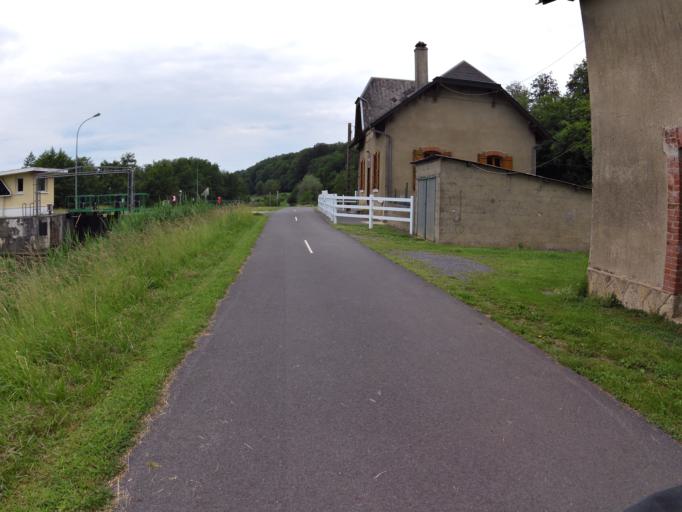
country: FR
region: Champagne-Ardenne
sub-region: Departement des Ardennes
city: Saint-Laurent
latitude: 49.7531
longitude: 4.7608
